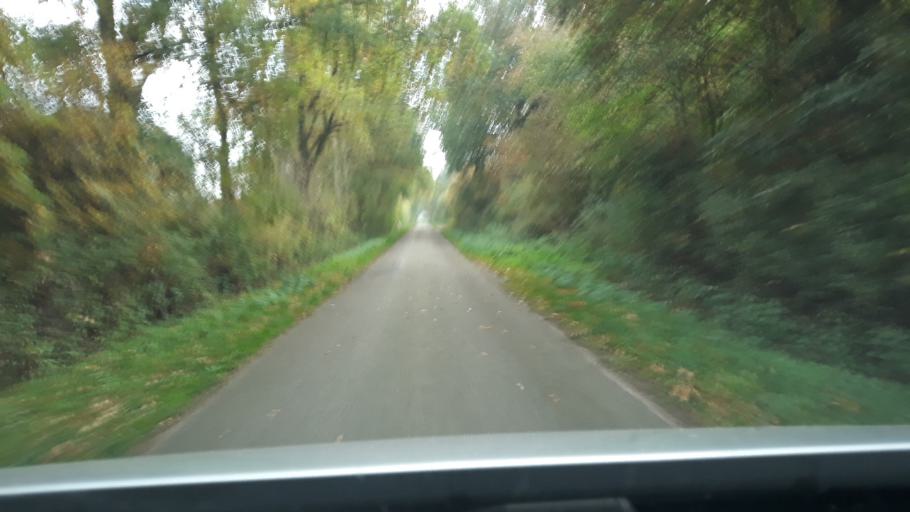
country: DE
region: Schleswig-Holstein
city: Klein Bennebek
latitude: 54.4051
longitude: 9.4710
